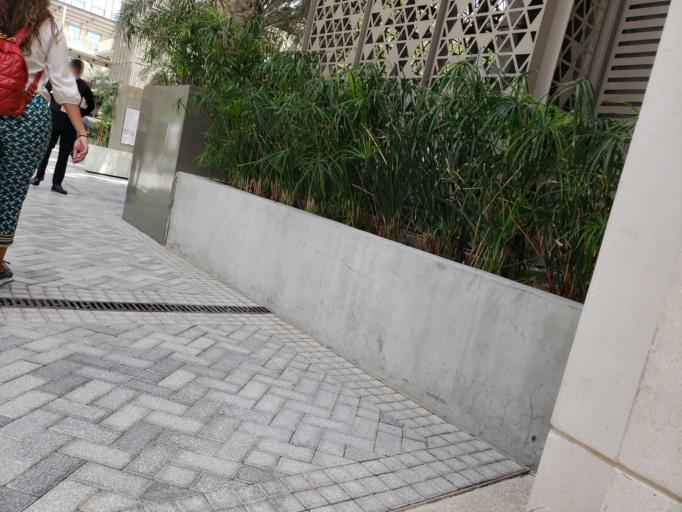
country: AE
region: Dubai
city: Dubai
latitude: 24.9597
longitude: 55.1492
